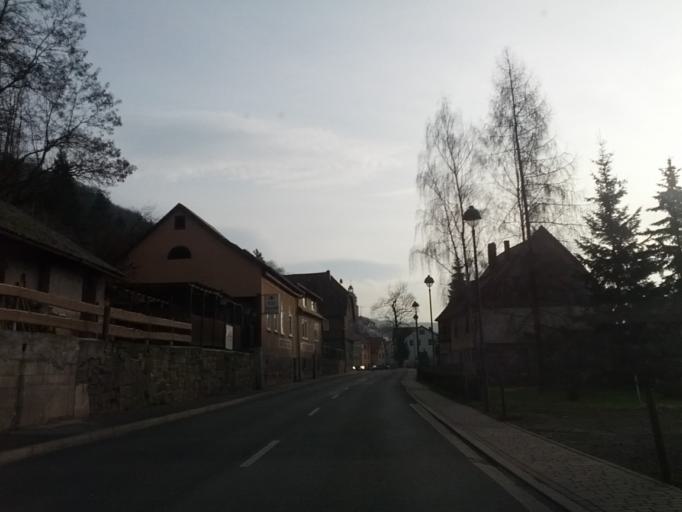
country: DE
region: Thuringia
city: Wasungen
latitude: 50.6672
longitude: 10.3639
